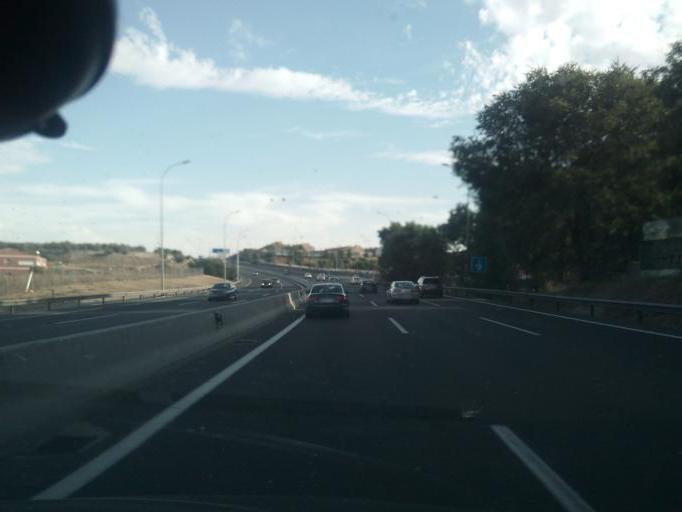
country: ES
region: Madrid
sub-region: Provincia de Madrid
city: Valdemoro
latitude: 40.1892
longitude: -3.6721
